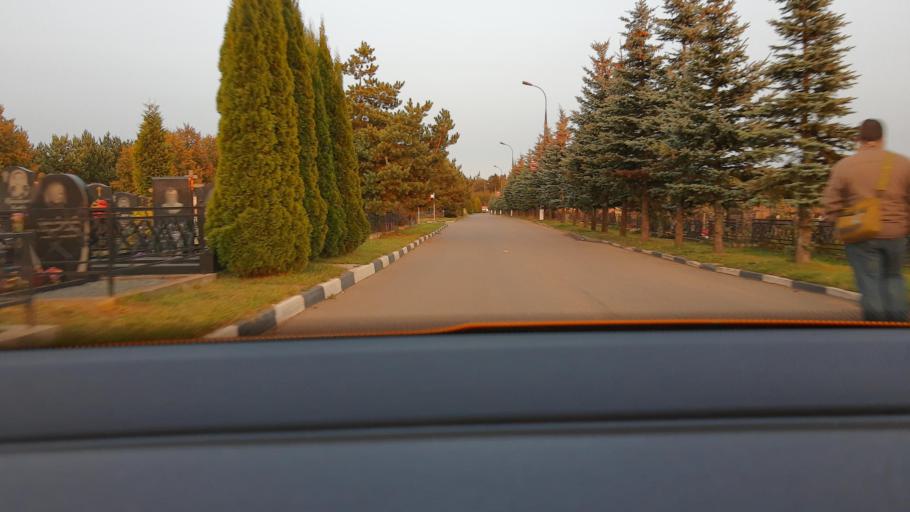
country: RU
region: Moskovskaya
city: Novopodrezkovo
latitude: 56.0063
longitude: 37.3893
